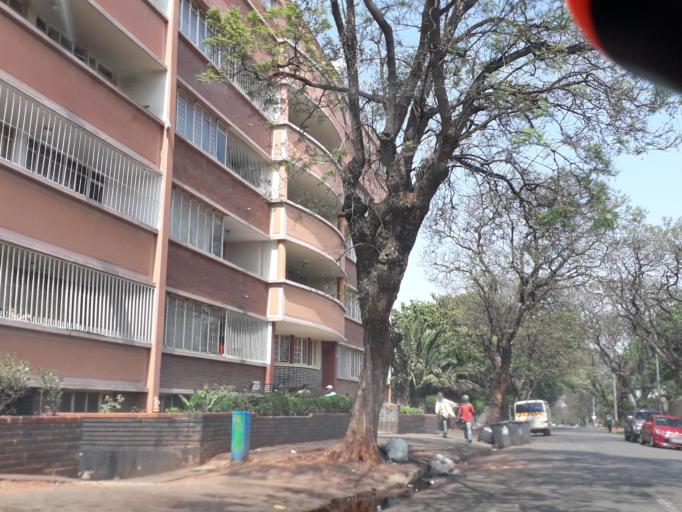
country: ZA
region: Gauteng
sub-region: City of Johannesburg Metropolitan Municipality
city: Johannesburg
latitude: -26.1777
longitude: 28.0662
